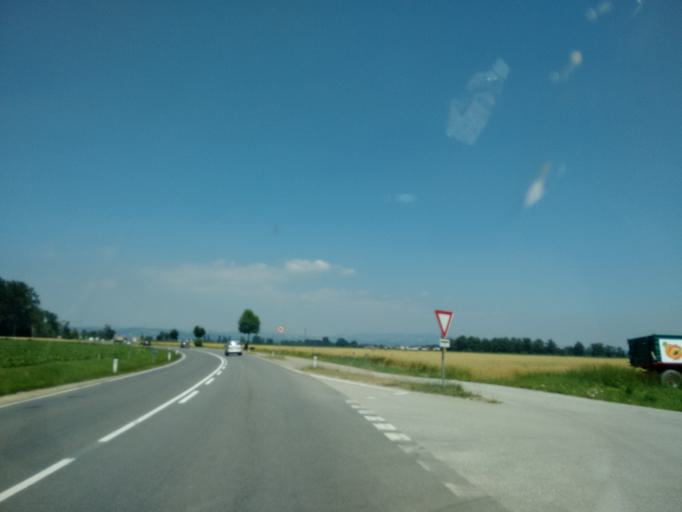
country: AT
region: Upper Austria
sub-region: Wels-Land
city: Buchkirchen
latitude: 48.2847
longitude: 14.0060
